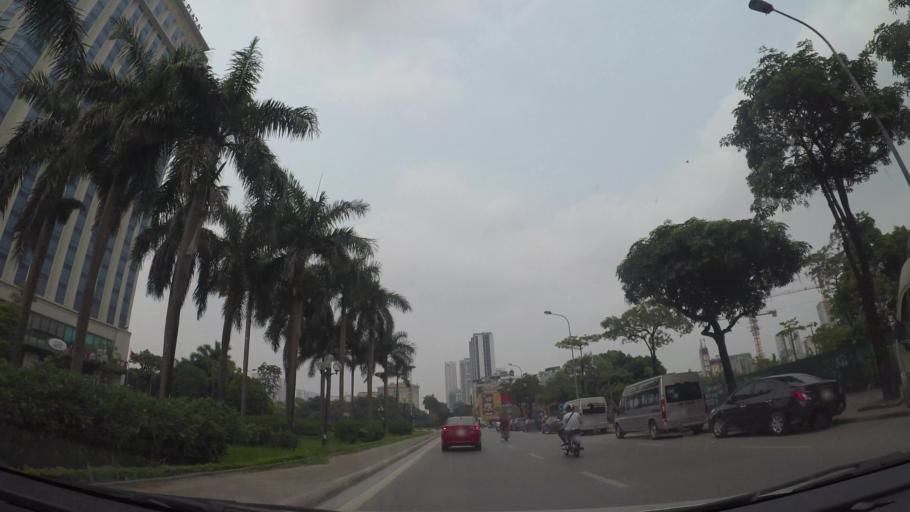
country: VN
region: Ha Noi
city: Cau Dien
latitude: 21.0269
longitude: 105.7681
